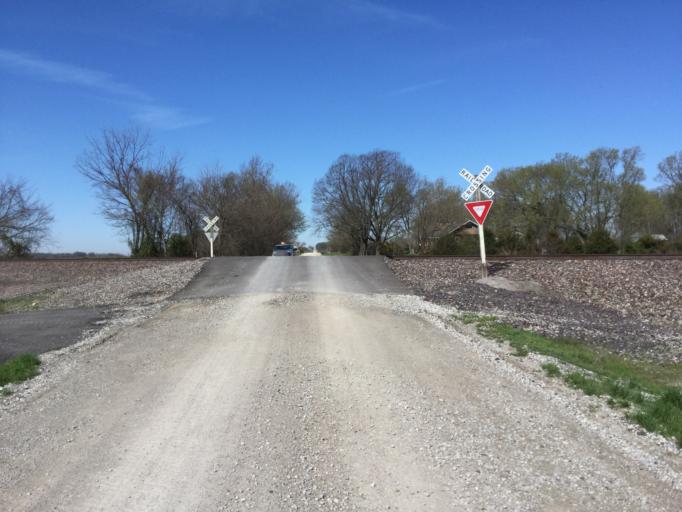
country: US
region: Kansas
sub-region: Neosho County
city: Erie
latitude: 37.6161
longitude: -95.2064
